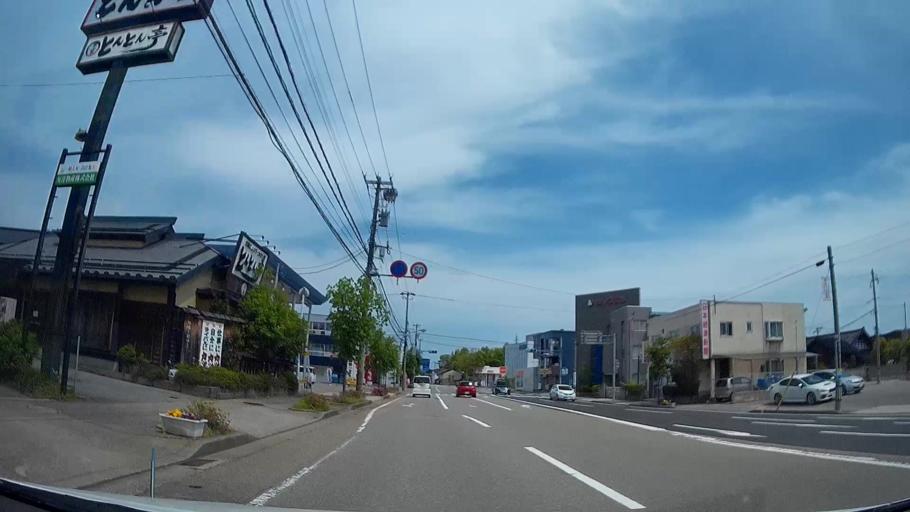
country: JP
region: Ishikawa
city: Kanazawa-shi
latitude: 36.5842
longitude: 136.6482
